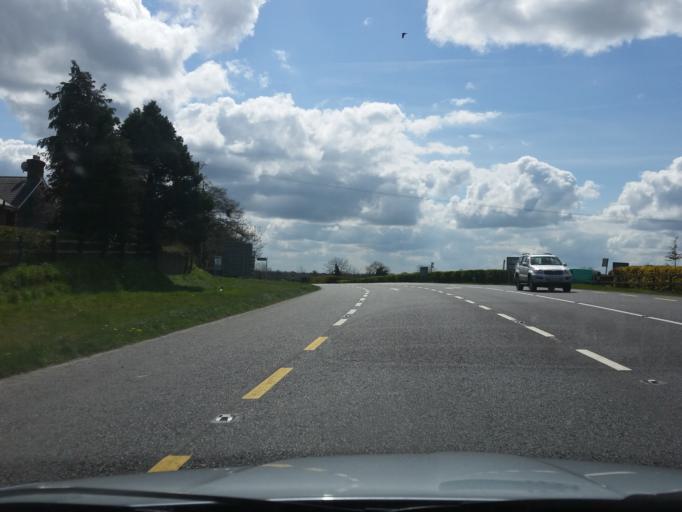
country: IE
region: Leinster
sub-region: An Mhi
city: Slane
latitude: 53.6860
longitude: -6.5417
